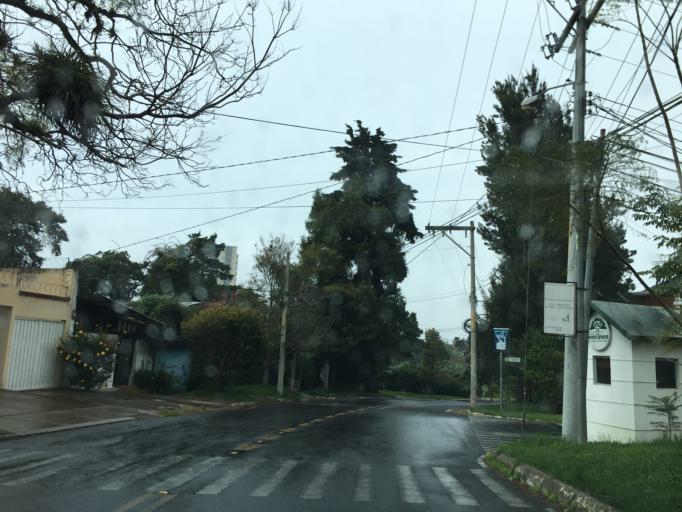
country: GT
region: Guatemala
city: Santa Catarina Pinula
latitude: 14.5851
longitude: -90.4930
